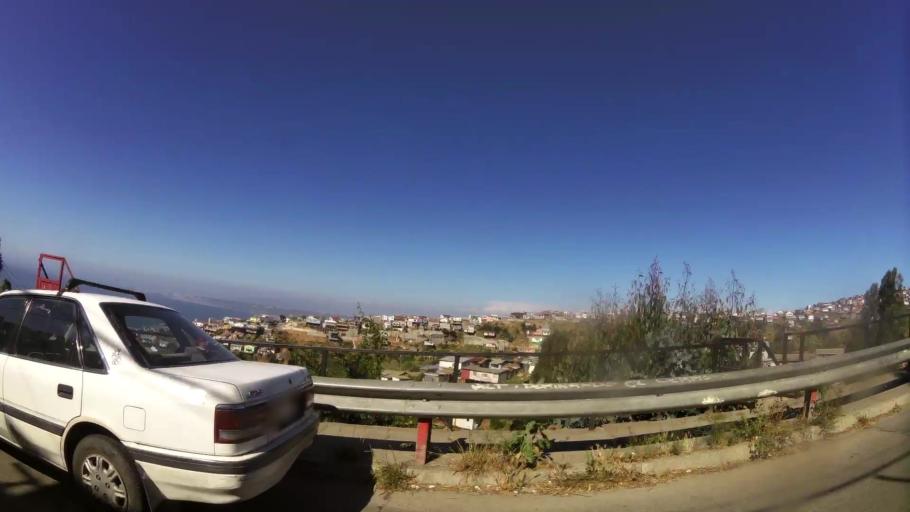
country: CL
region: Valparaiso
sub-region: Provincia de Valparaiso
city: Valparaiso
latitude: -33.0610
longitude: -71.6184
